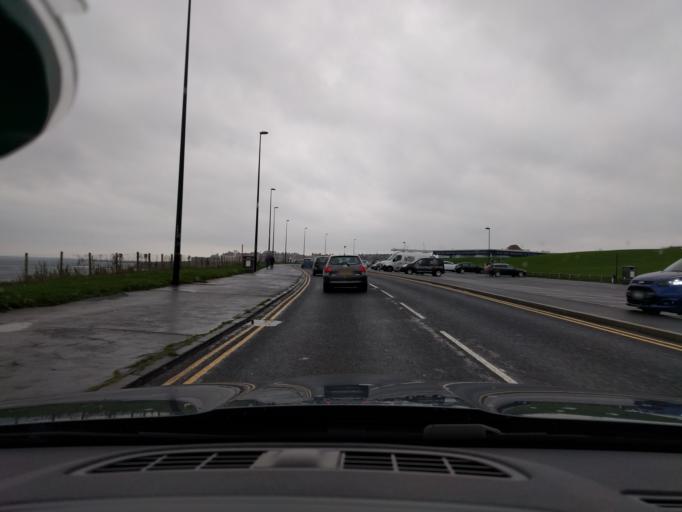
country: GB
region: England
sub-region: Borough of North Tyneside
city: Tynemouth
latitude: 55.0297
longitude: -1.4306
